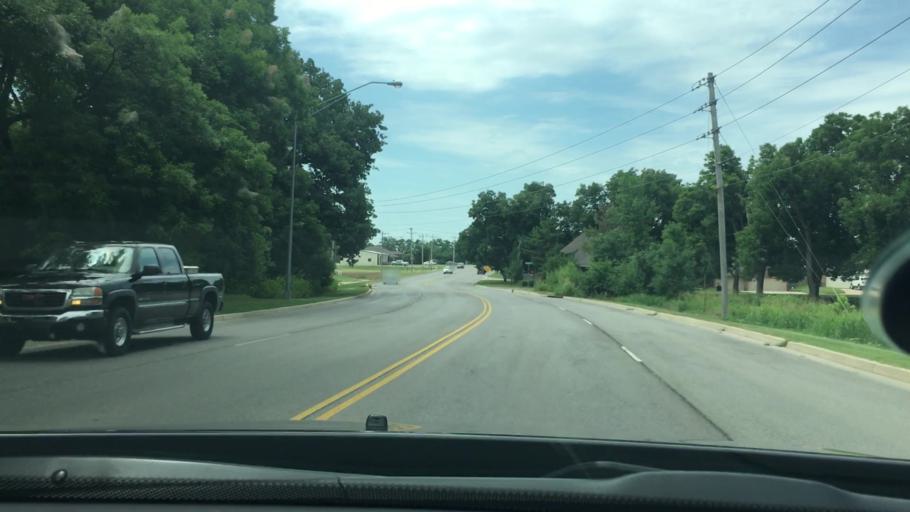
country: US
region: Oklahoma
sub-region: Carter County
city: Ardmore
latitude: 34.1824
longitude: -97.1608
